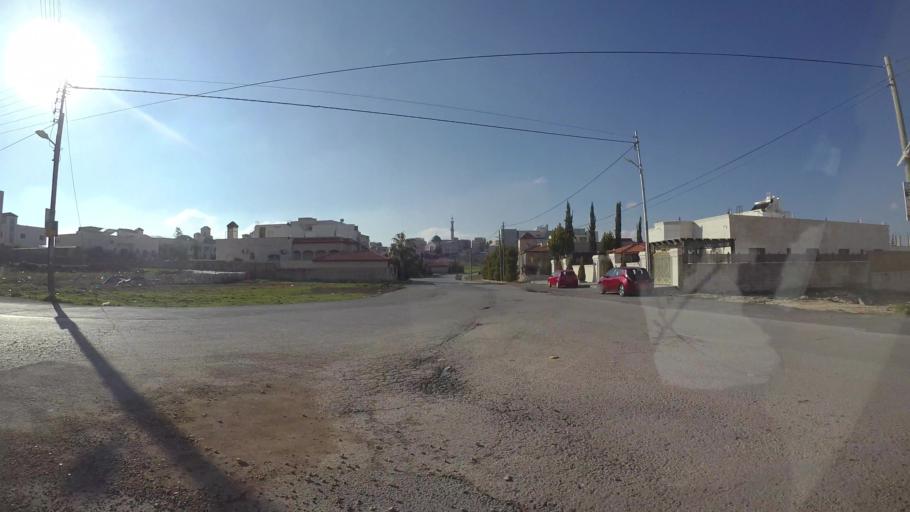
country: JO
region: Amman
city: Al Bunayyat ash Shamaliyah
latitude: 31.9023
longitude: 35.9216
